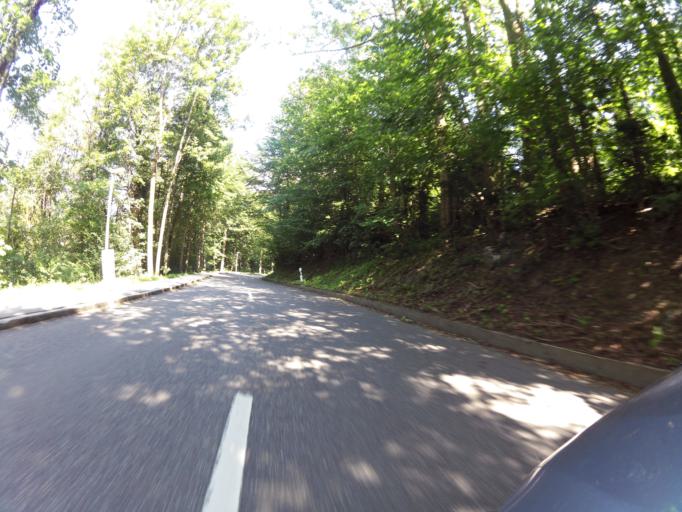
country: DE
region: Bavaria
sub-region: Upper Bavaria
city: Berchtesgaden
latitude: 47.6230
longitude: 12.9887
